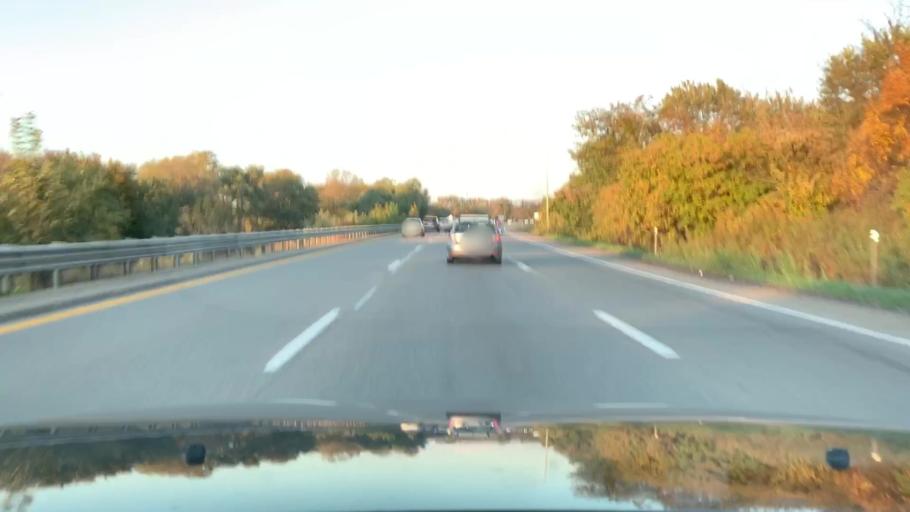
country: US
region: Michigan
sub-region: Kent County
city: Grandville
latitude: 42.9189
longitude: -85.7607
